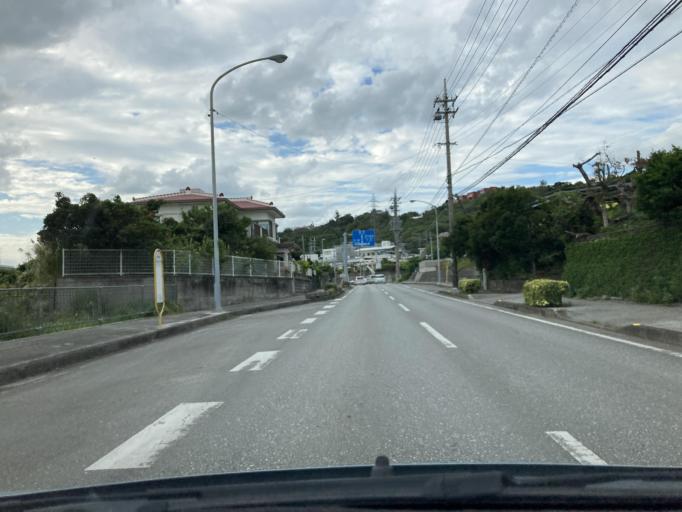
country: JP
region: Okinawa
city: Gushikawa
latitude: 26.3485
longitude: 127.8641
